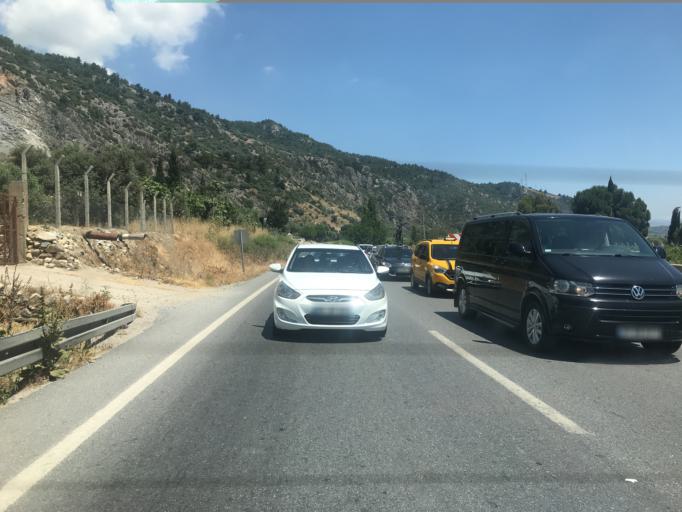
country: TR
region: Aydin
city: Soeke
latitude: 37.7927
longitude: 27.4663
